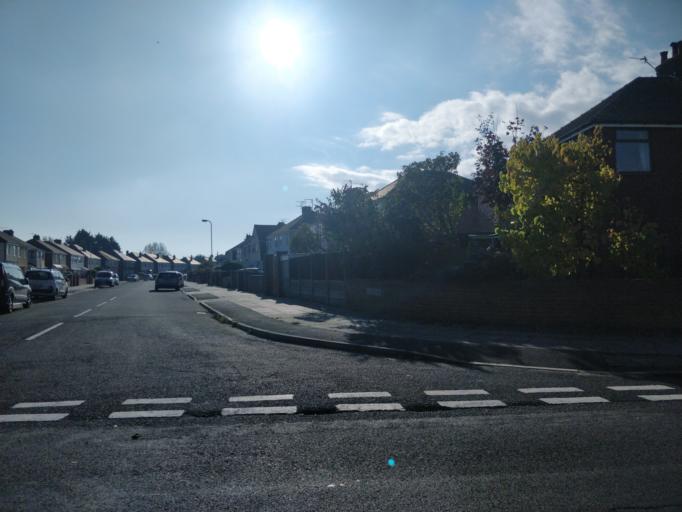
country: GB
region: England
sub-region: Lancashire
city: Banks
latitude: 53.6691
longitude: -2.9545
